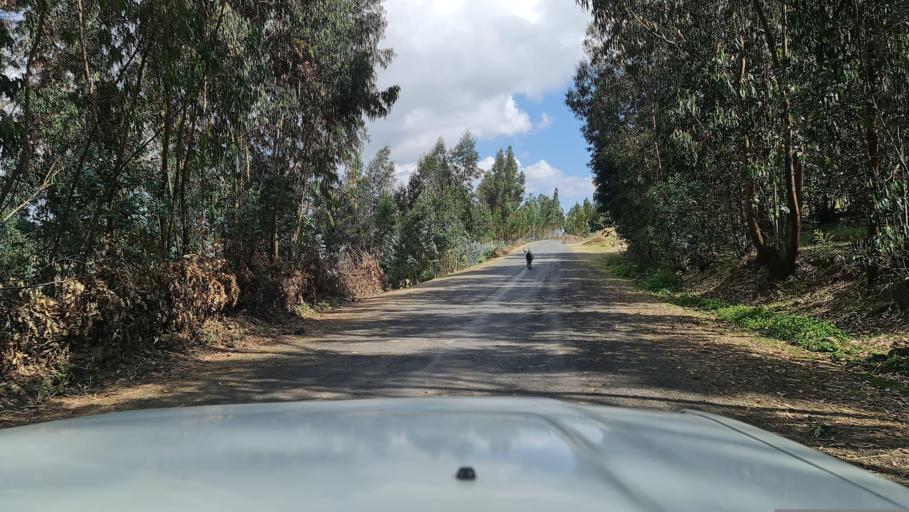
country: ET
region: Amhara
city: Debark'
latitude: 13.1409
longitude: 37.9178
